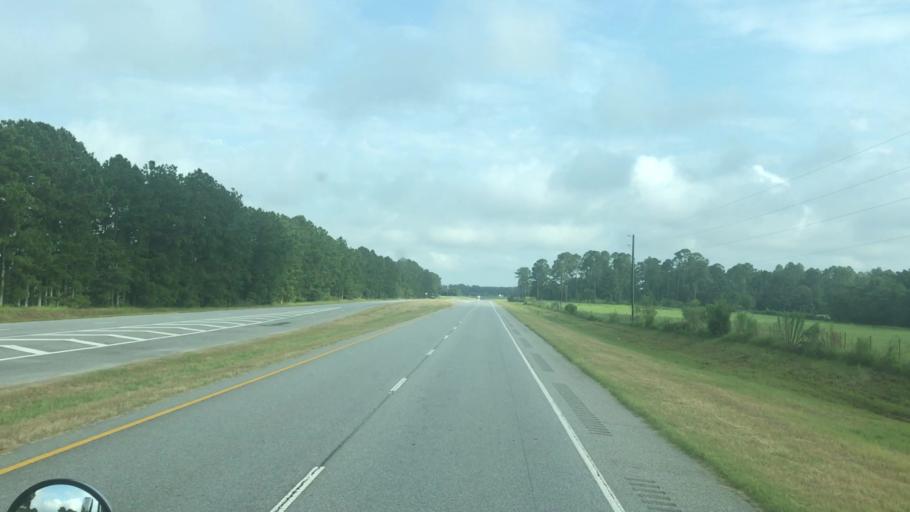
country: US
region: Georgia
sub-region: Miller County
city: Colquitt
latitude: 31.2095
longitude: -84.7737
